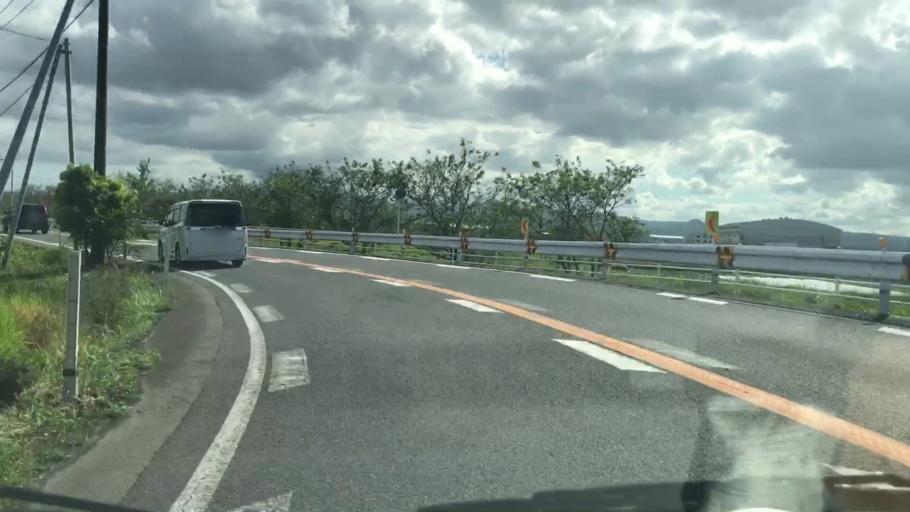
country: JP
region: Saga Prefecture
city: Kashima
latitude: 33.1644
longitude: 130.1682
